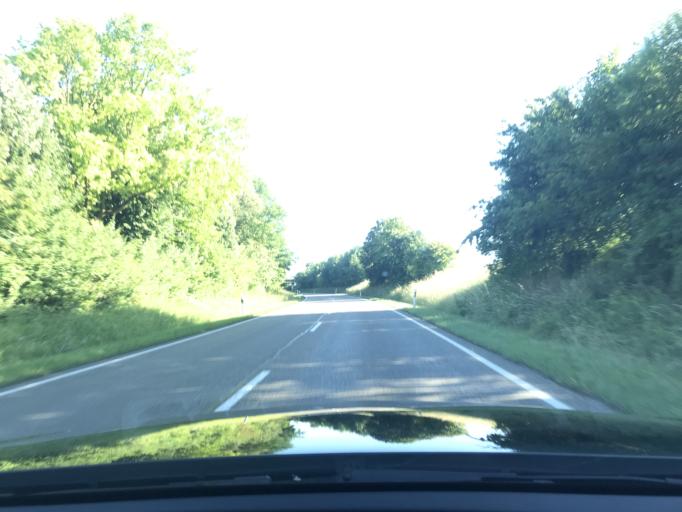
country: DE
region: Baden-Wuerttemberg
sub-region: Regierungsbezirk Stuttgart
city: Stuttgart Muehlhausen
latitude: 48.8448
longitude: 9.2519
